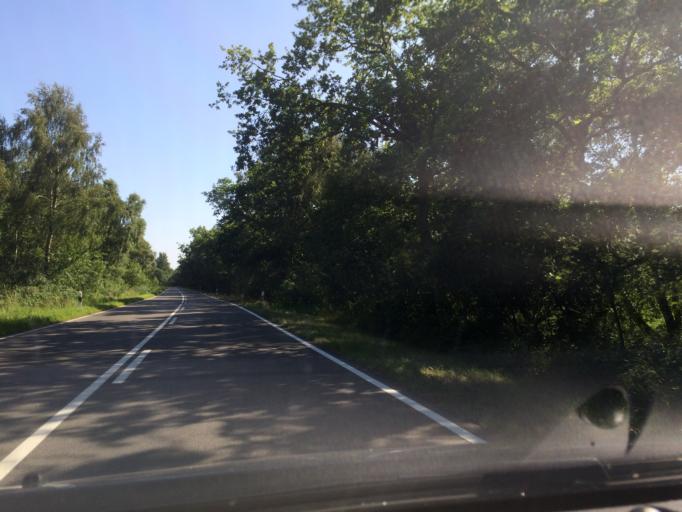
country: DE
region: Mecklenburg-Vorpommern
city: Zingst
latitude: 54.4270
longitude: 12.6510
